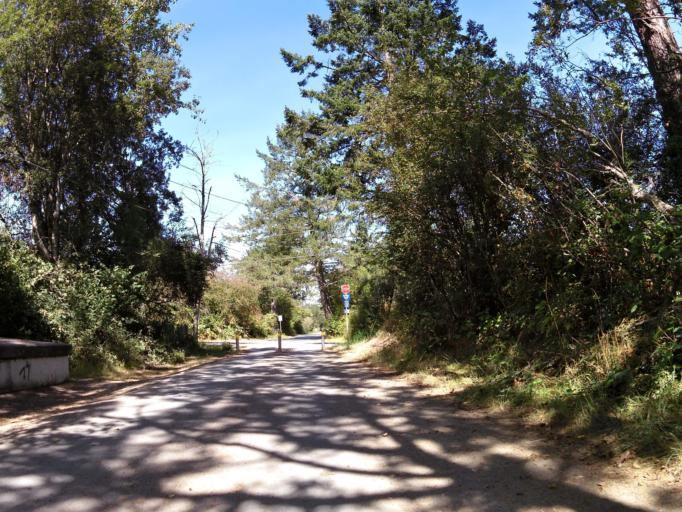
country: CA
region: British Columbia
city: Victoria
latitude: 48.5504
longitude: -123.3856
